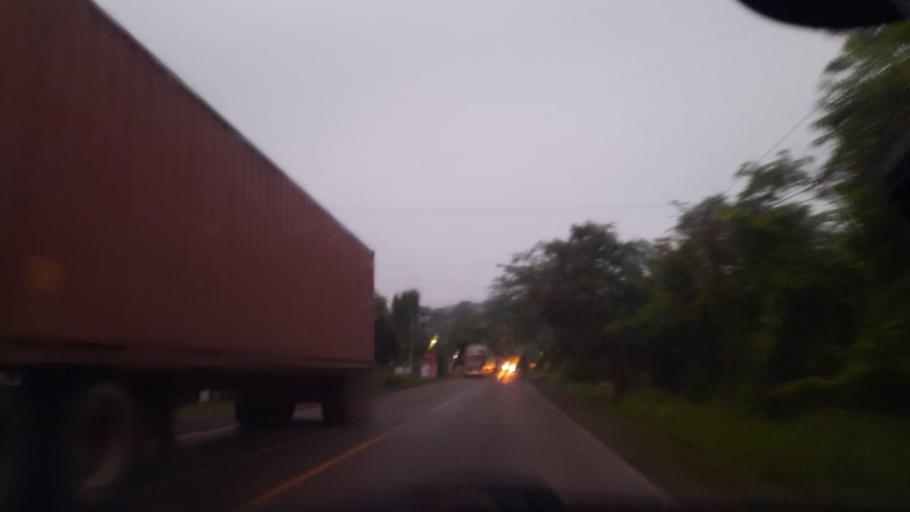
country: GT
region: Jutiapa
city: Atescatempa
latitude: 14.2085
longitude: -89.6807
